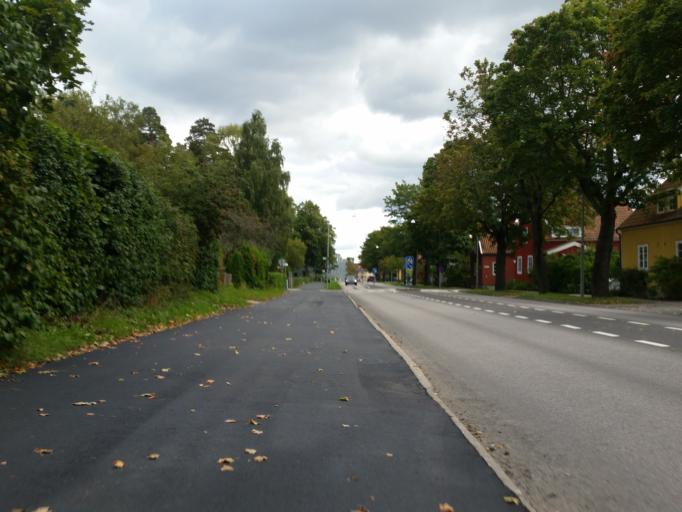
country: SE
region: Stockholm
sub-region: Stockholms Kommun
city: Arsta
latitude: 59.2826
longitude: 18.1032
